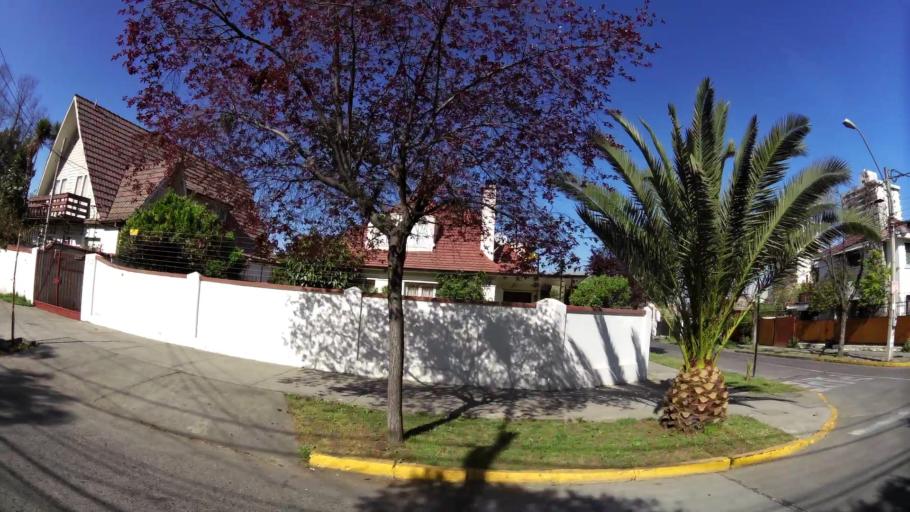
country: CL
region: Santiago Metropolitan
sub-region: Provincia de Santiago
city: Villa Presidente Frei, Nunoa, Santiago, Chile
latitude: -33.4340
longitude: -70.5844
